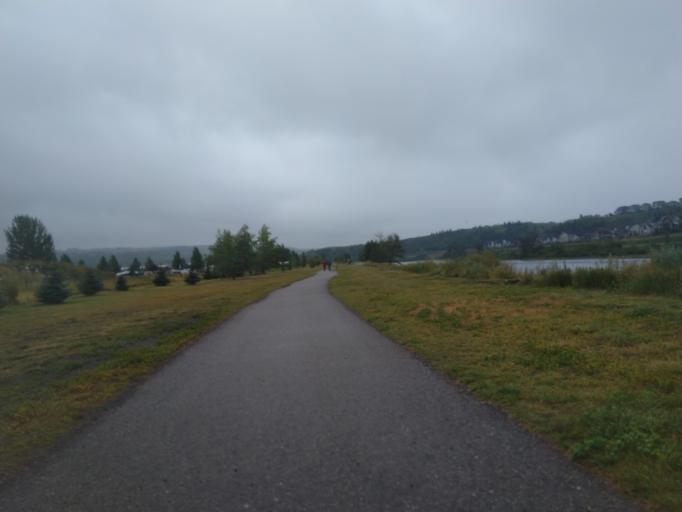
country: CA
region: Alberta
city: Cochrane
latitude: 51.1742
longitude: -114.4622
